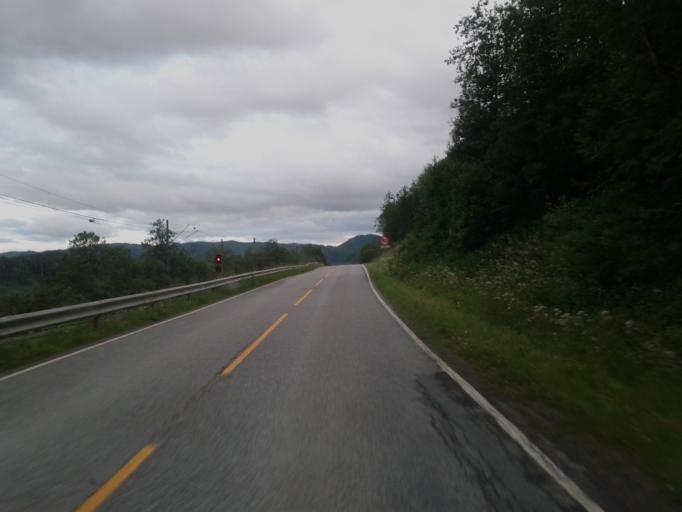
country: NO
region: Sor-Trondelag
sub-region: Midtre Gauldal
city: Storen
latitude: 63.0610
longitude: 10.2881
